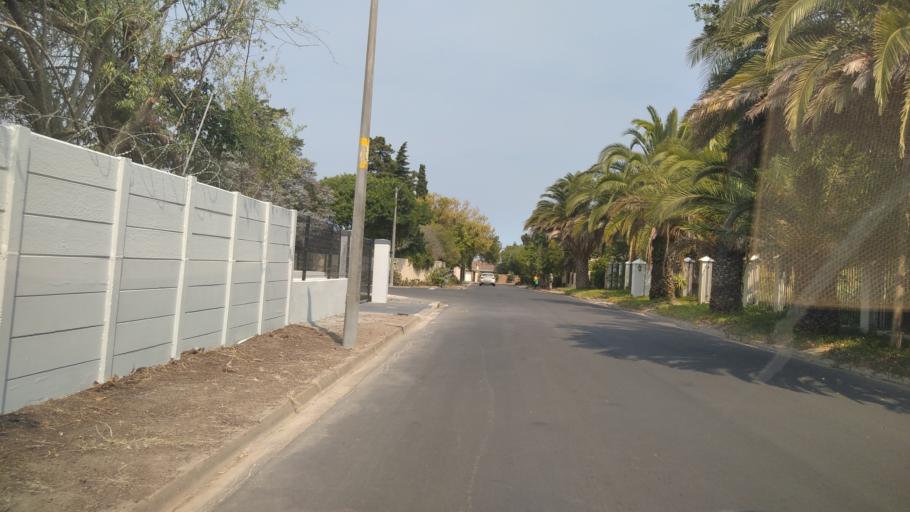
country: ZA
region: Western Cape
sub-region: City of Cape Town
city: Kraaifontein
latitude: -33.8238
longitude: 18.6513
